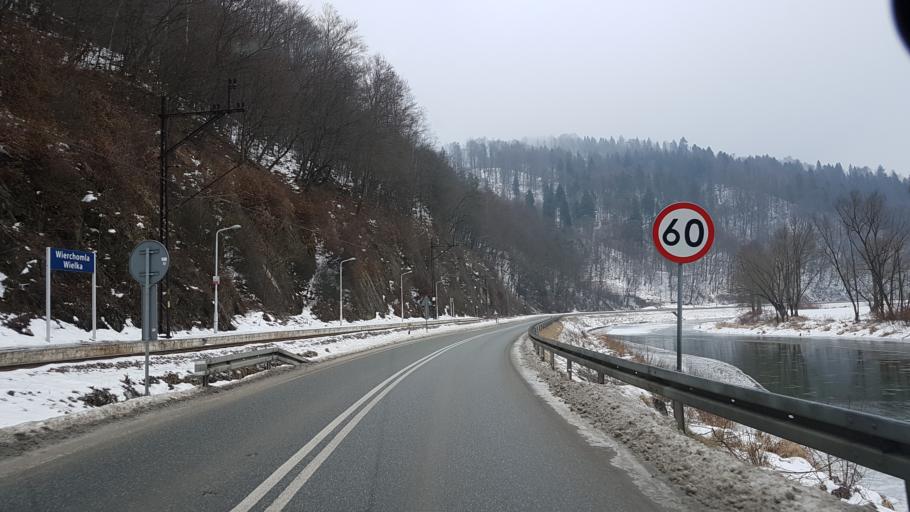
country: PL
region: Lesser Poland Voivodeship
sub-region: Powiat nowosadecki
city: Piwniczna-Zdroj
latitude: 49.4024
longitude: 20.7555
